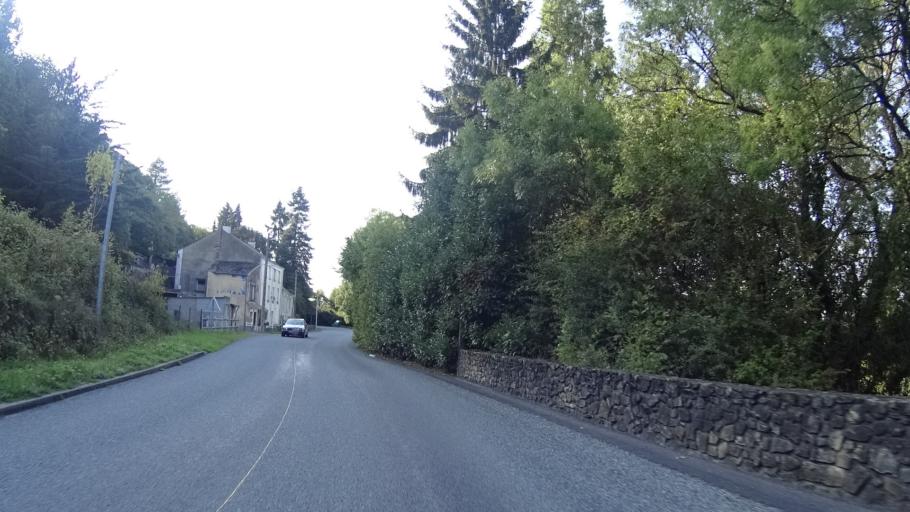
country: FR
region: Pays de la Loire
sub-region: Departement de Maine-et-Loire
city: La Possonniere
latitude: 47.3462
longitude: -0.7175
